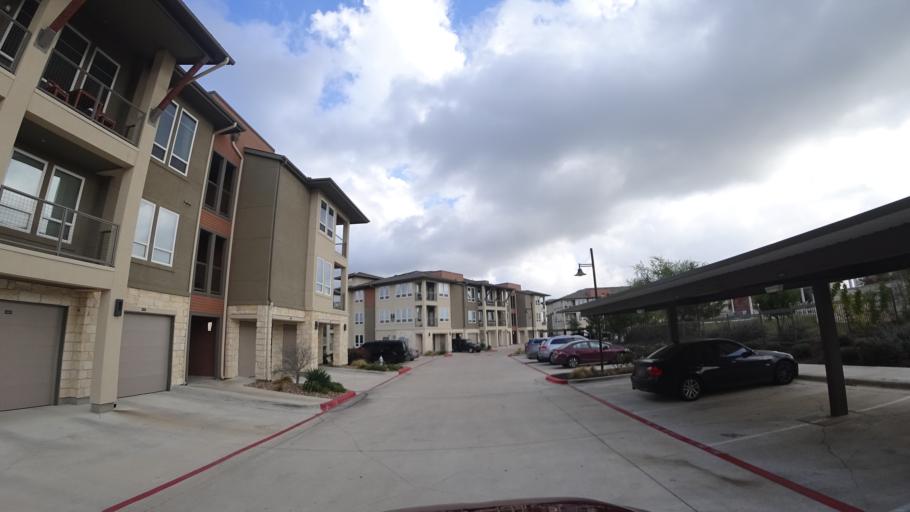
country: US
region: Texas
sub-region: Travis County
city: Hudson Bend
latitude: 30.3835
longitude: -97.8744
